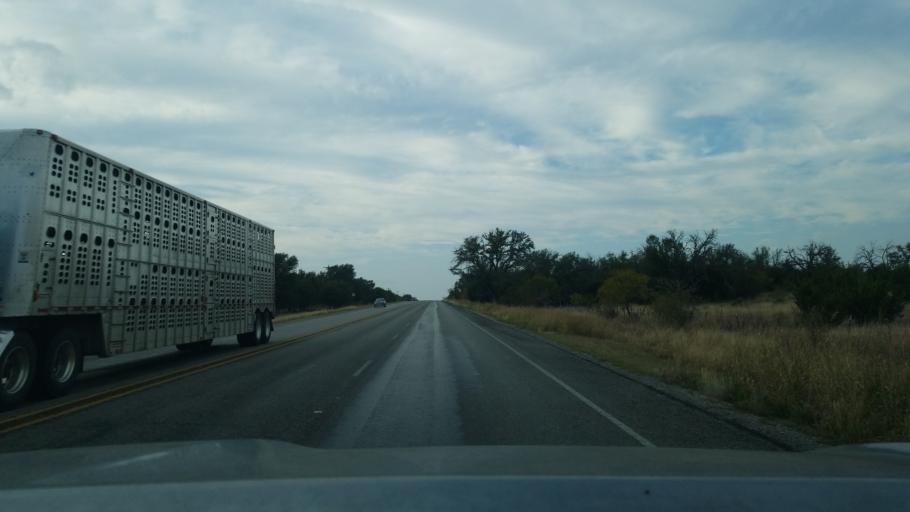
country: US
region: Texas
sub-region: Mills County
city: Goldthwaite
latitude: 31.5353
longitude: -98.6175
